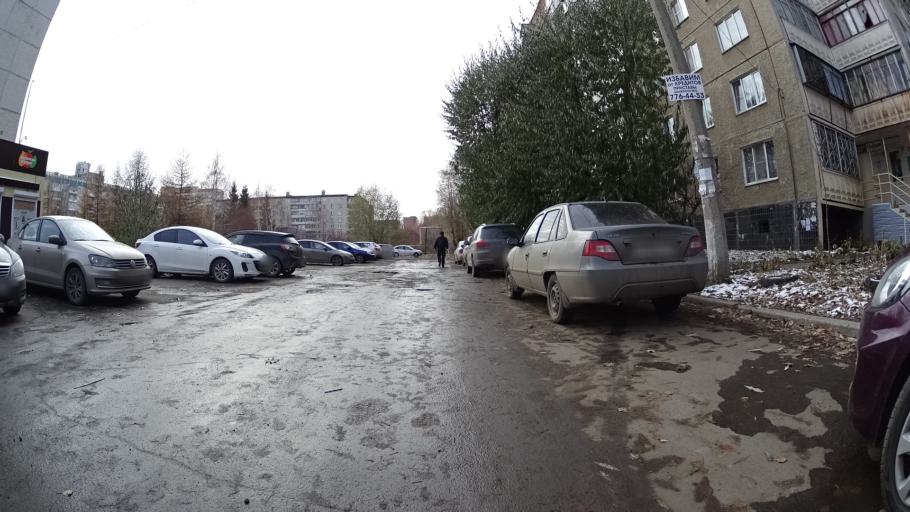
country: RU
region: Chelyabinsk
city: Roshchino
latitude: 55.1896
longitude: 61.3007
